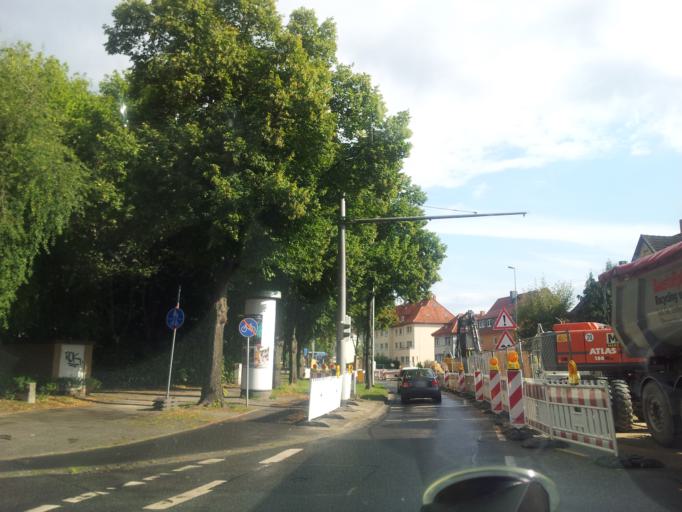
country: DE
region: Lower Saxony
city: Braunschweig
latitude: 52.2423
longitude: 10.5358
